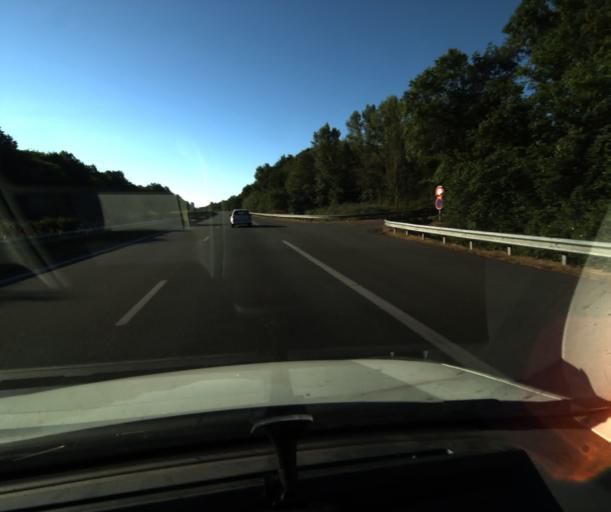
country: FR
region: Midi-Pyrenees
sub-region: Departement du Tarn-et-Garonne
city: Montech
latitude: 43.9934
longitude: 1.2321
